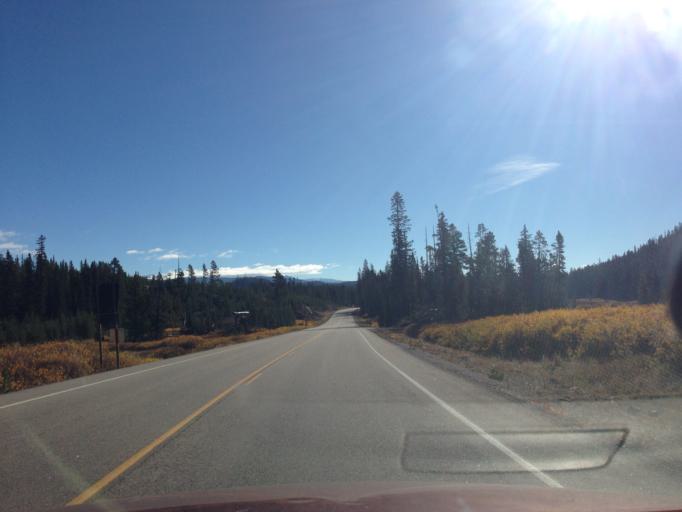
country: US
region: Montana
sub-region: Carbon County
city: Red Lodge
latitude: 45.0267
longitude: -109.8908
